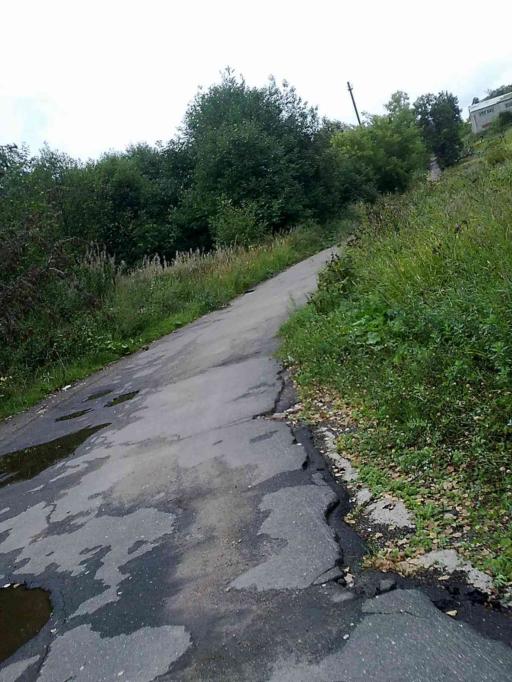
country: RU
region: Moskovskaya
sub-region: Leninskiy Rayon
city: Vnukovo
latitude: 55.6281
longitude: 37.2631
